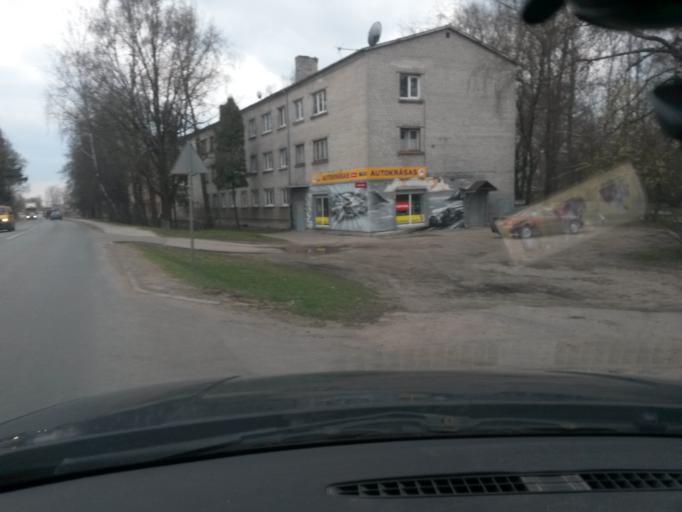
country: LV
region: Kekava
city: Kekava
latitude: 56.8962
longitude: 24.2270
